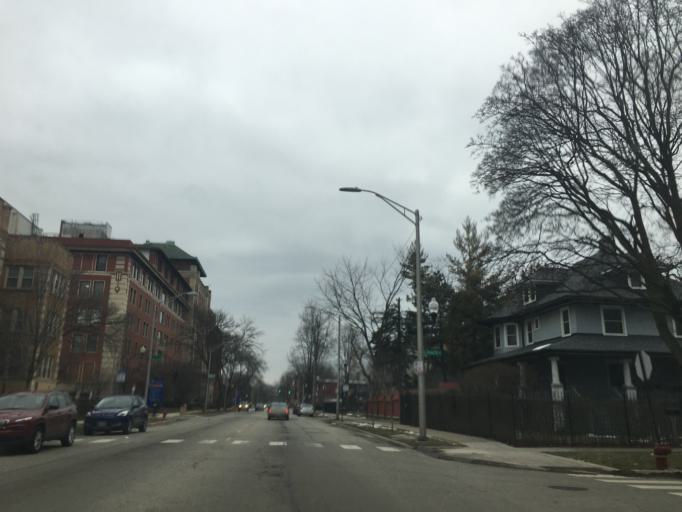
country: US
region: Illinois
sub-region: Cook County
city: Oak Park
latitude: 41.8899
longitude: -87.7750
